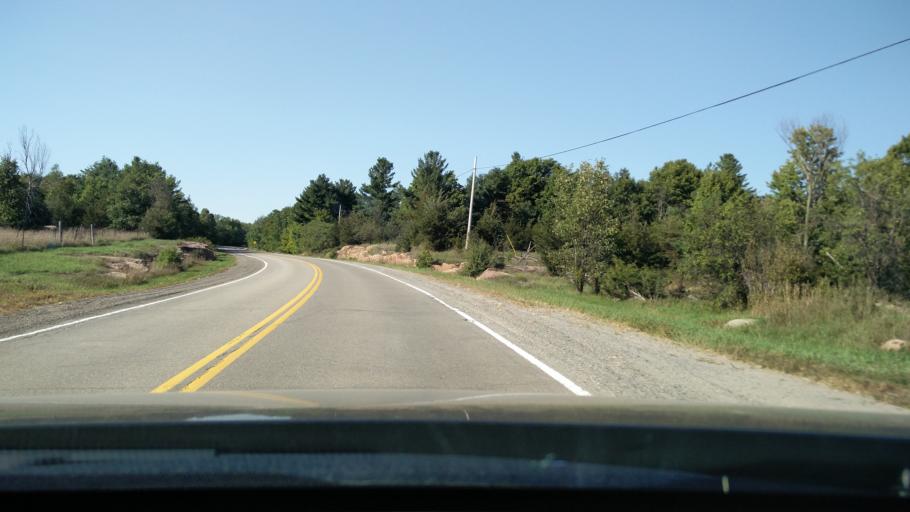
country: CA
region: Ontario
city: Perth
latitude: 44.7050
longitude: -76.3996
